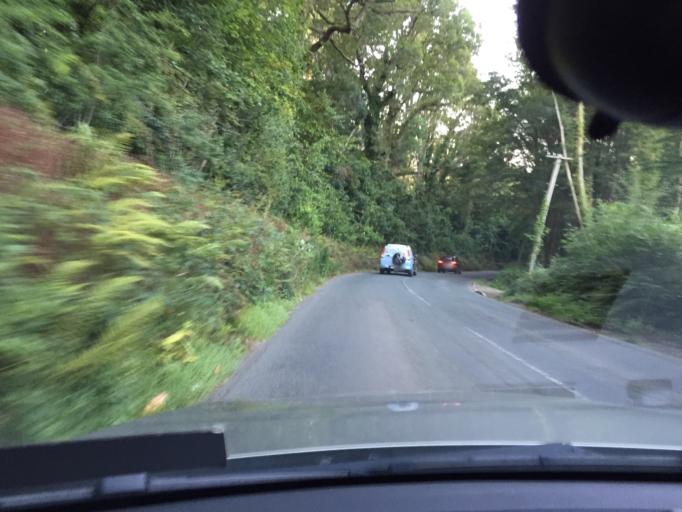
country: IE
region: Leinster
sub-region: Wicklow
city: Enniskerry
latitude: 53.1769
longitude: -6.1757
